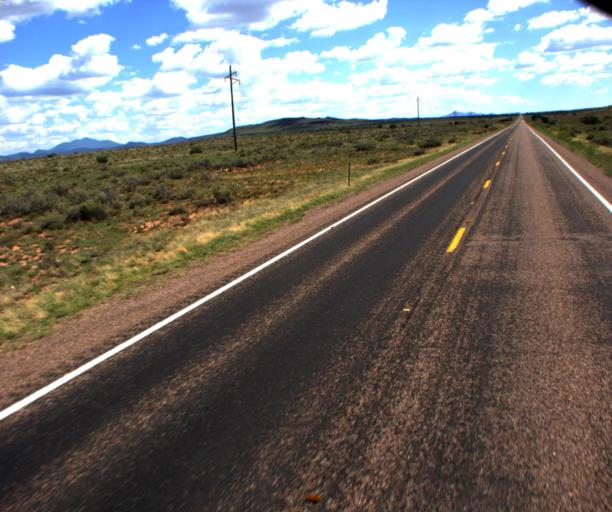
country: US
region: Arizona
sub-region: Coconino County
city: Williams
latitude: 35.5795
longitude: -112.1527
